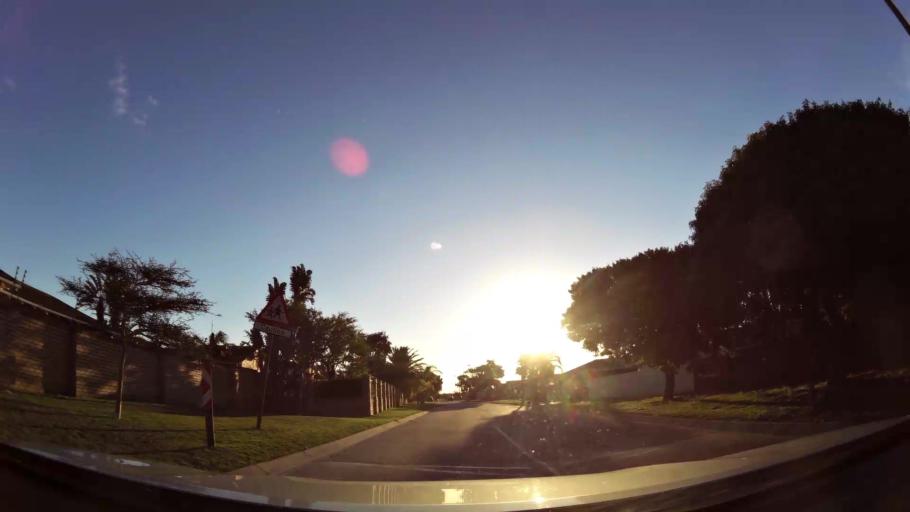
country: ZA
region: Eastern Cape
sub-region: Nelson Mandela Bay Metropolitan Municipality
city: Port Elizabeth
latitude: -33.9667
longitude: 25.4889
